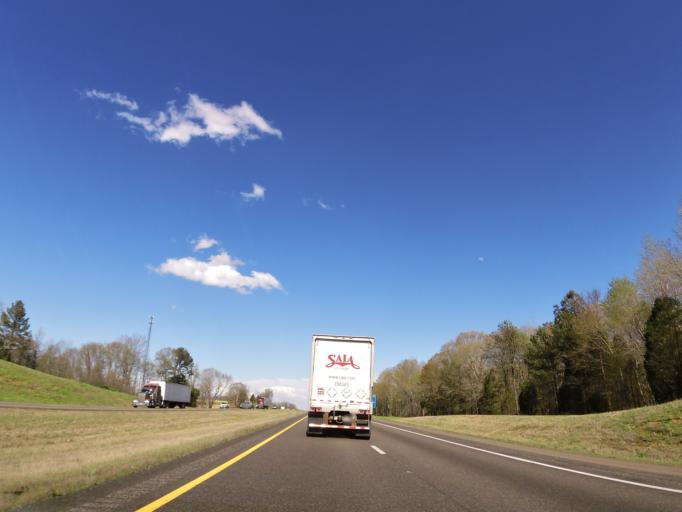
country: US
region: Tennessee
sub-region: Henderson County
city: Lexington
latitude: 35.7796
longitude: -88.4198
